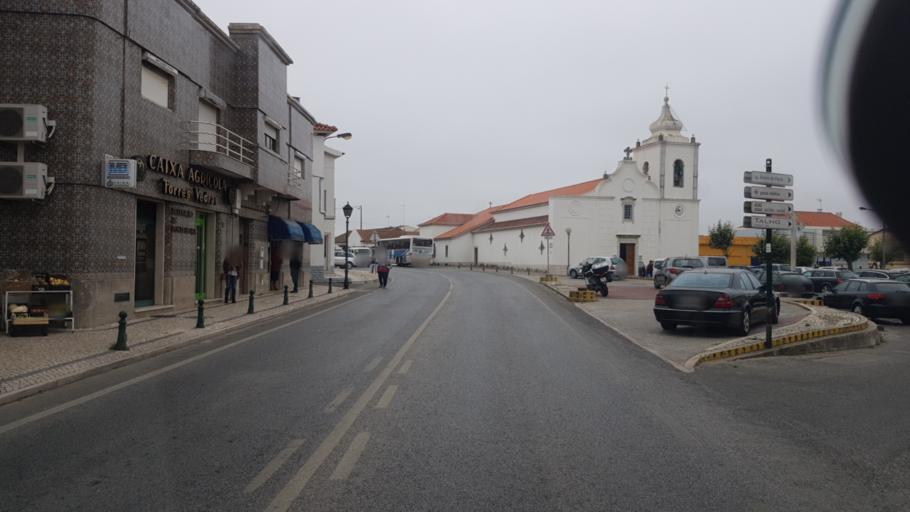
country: PT
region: Lisbon
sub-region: Torres Vedras
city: Silveira
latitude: 39.0908
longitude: -9.3199
